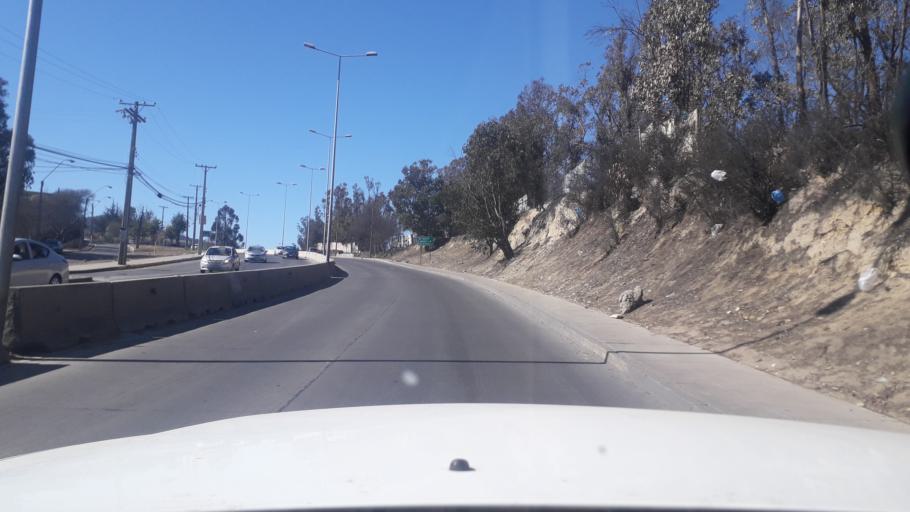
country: CL
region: Valparaiso
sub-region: Provincia de Valparaiso
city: Vina del Mar
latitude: -33.0385
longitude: -71.5050
